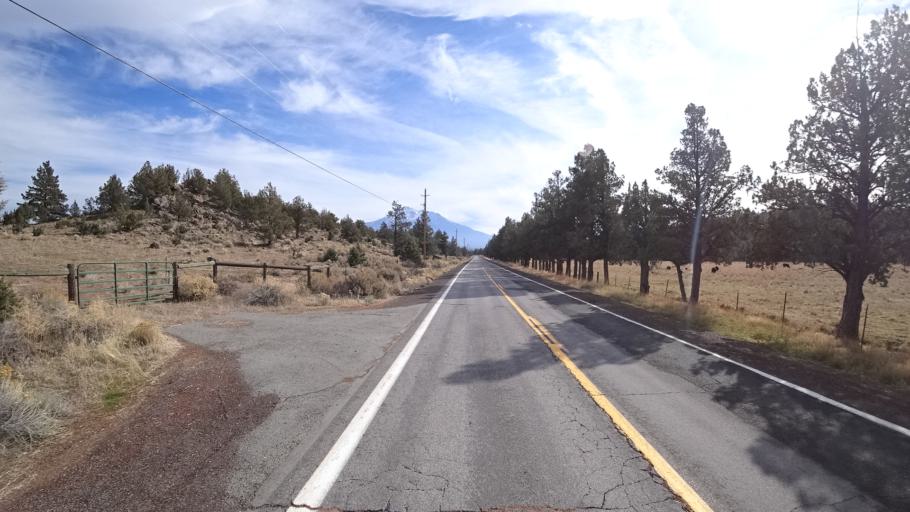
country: US
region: California
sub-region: Siskiyou County
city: Weed
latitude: 41.5796
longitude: -122.3979
